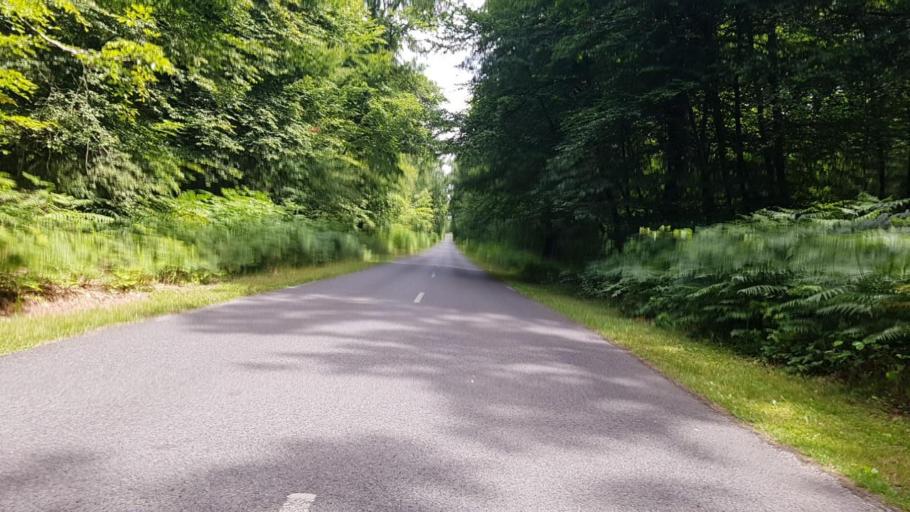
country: FR
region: Picardie
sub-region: Departement de l'Oise
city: Montmacq
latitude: 49.4772
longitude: 2.9226
